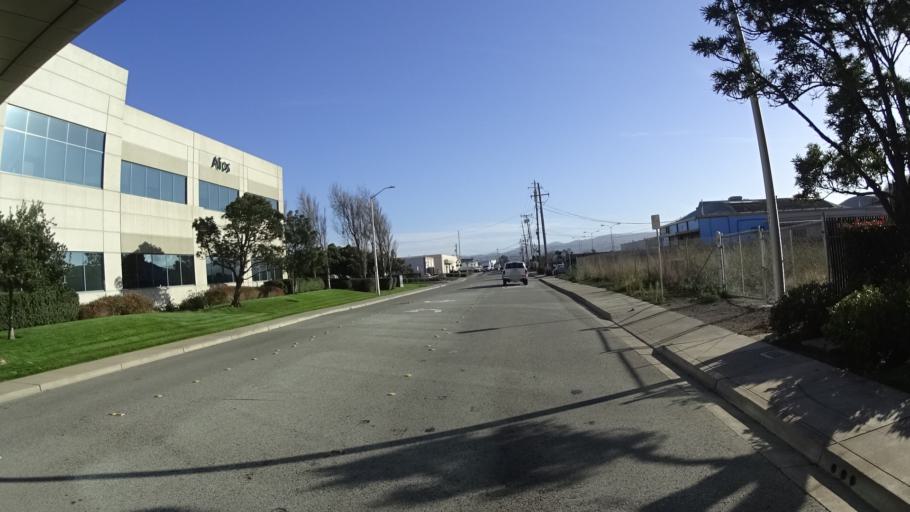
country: US
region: California
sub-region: San Mateo County
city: South San Francisco
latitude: 37.6527
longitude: -122.4002
